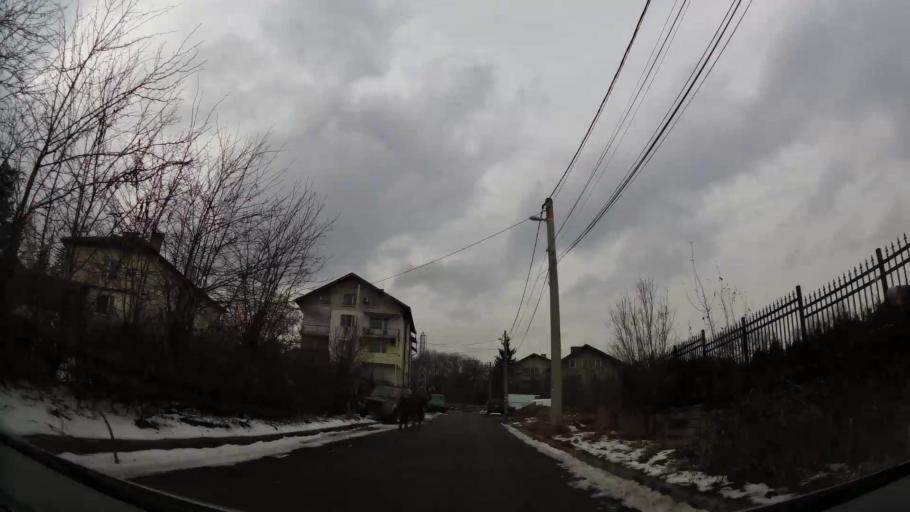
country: BG
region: Sofiya
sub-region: Obshtina Bozhurishte
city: Bozhurishte
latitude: 42.6778
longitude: 23.2345
